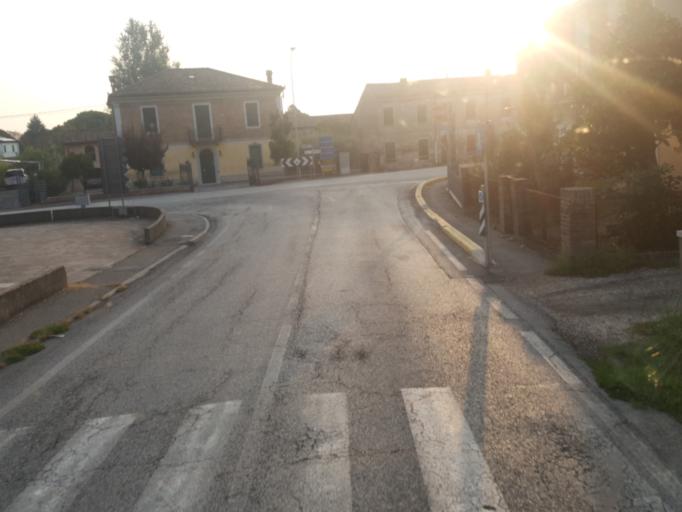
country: IT
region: Emilia-Romagna
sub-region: Provincia di Ravenna
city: Lavezzola
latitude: 44.5584
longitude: 11.8758
